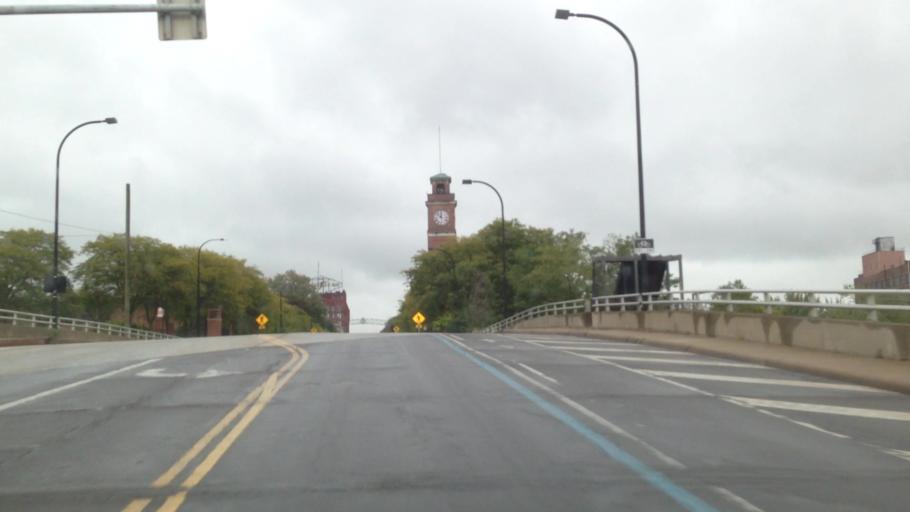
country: US
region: Ohio
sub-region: Summit County
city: Akron
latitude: 41.0698
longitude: -81.4875
